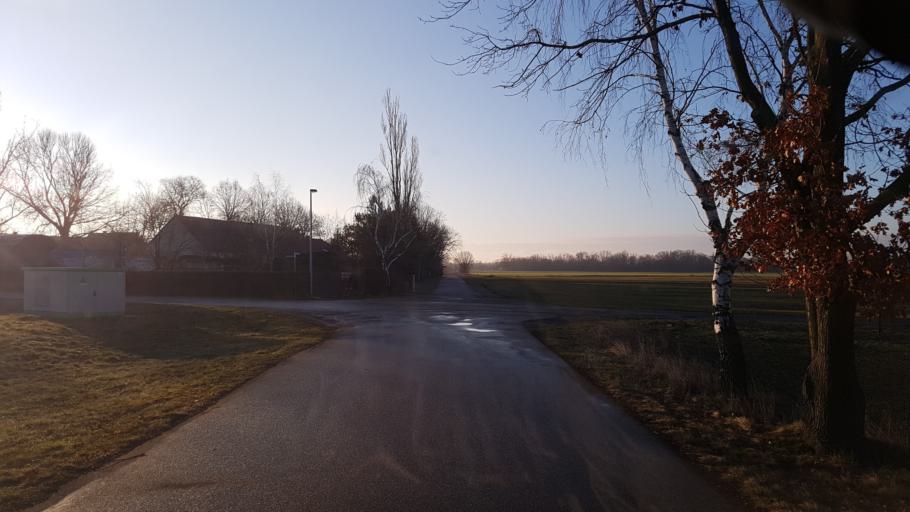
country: DE
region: Brandenburg
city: Falkenberg
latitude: 51.5630
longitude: 13.2220
